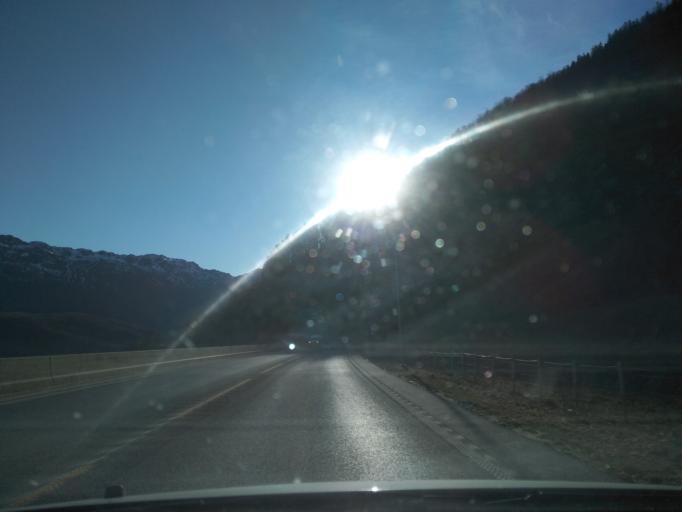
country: NO
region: Hordaland
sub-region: Etne
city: Etne
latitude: 59.7234
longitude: 6.1179
